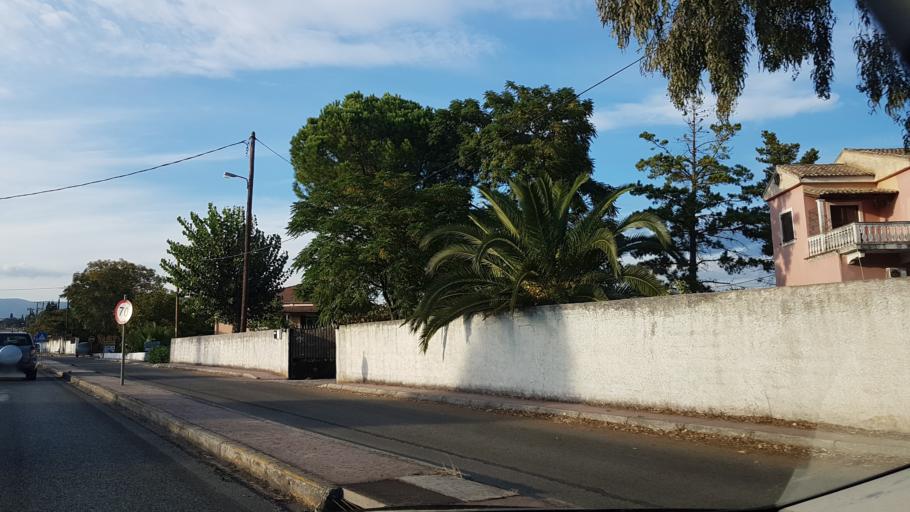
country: GR
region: Ionian Islands
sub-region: Nomos Kerkyras
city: Kontokali
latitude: 39.6509
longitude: 19.8437
